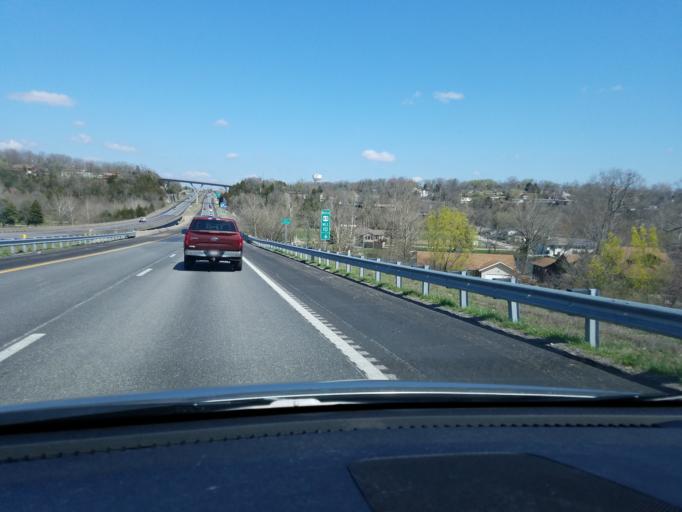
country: US
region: Missouri
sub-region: Taney County
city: Branson
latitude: 36.6320
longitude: -93.2246
